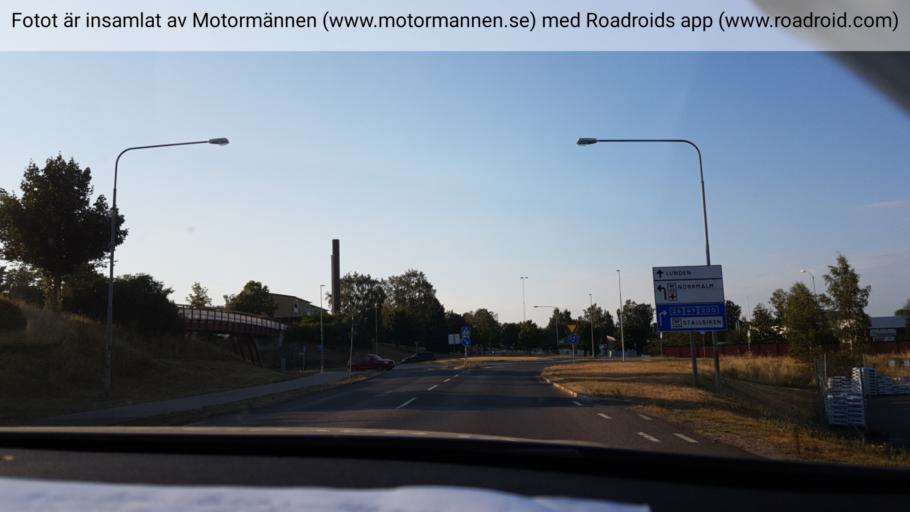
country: SE
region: Vaestra Goetaland
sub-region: Skovde Kommun
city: Skoevde
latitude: 58.4060
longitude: 13.8661
